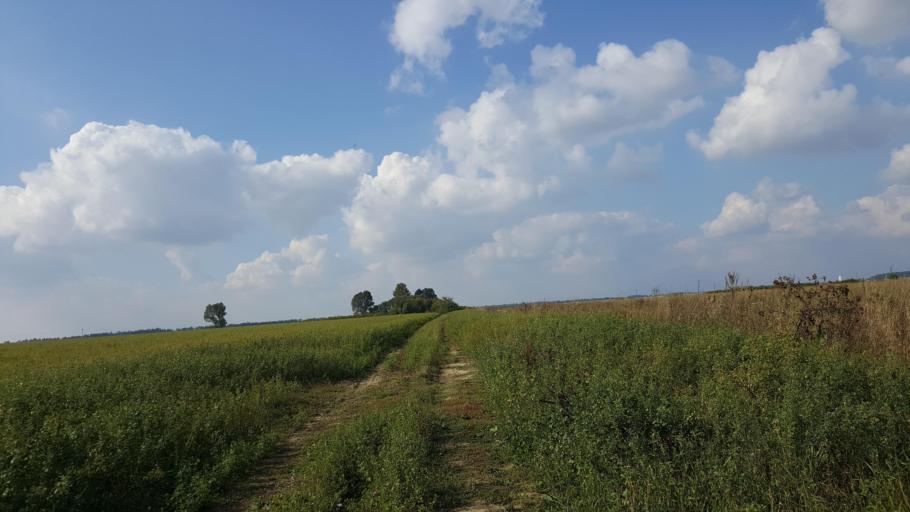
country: BY
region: Brest
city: Kamyanyets
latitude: 52.4202
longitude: 23.8133
